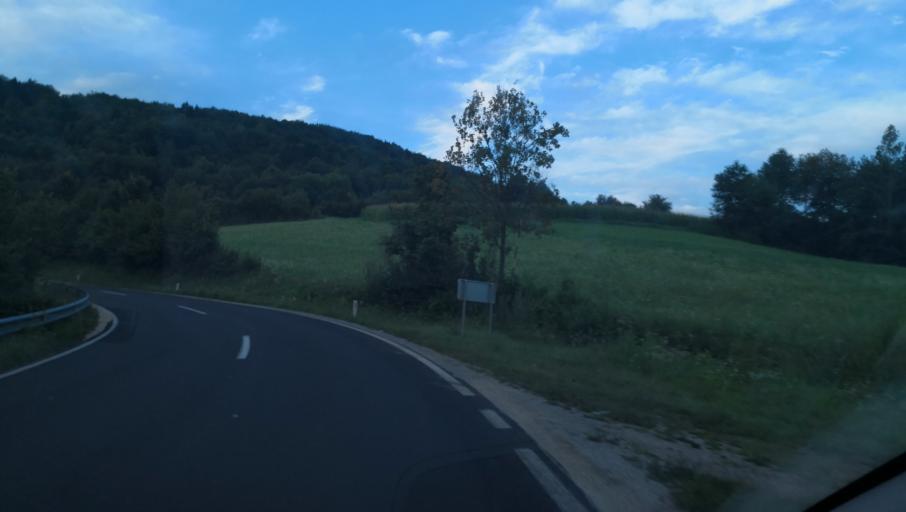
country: SI
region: Novo Mesto
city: Novo Mesto
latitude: 45.7370
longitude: 15.2204
